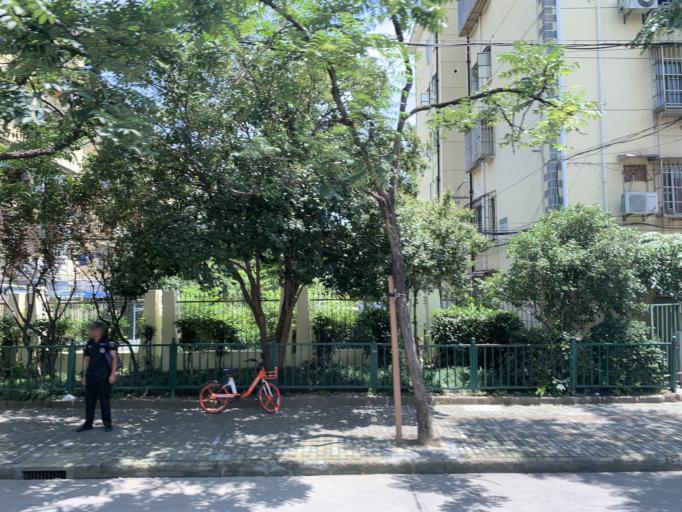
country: CN
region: Shanghai Shi
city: Huamu
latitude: 31.2493
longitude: 121.5753
